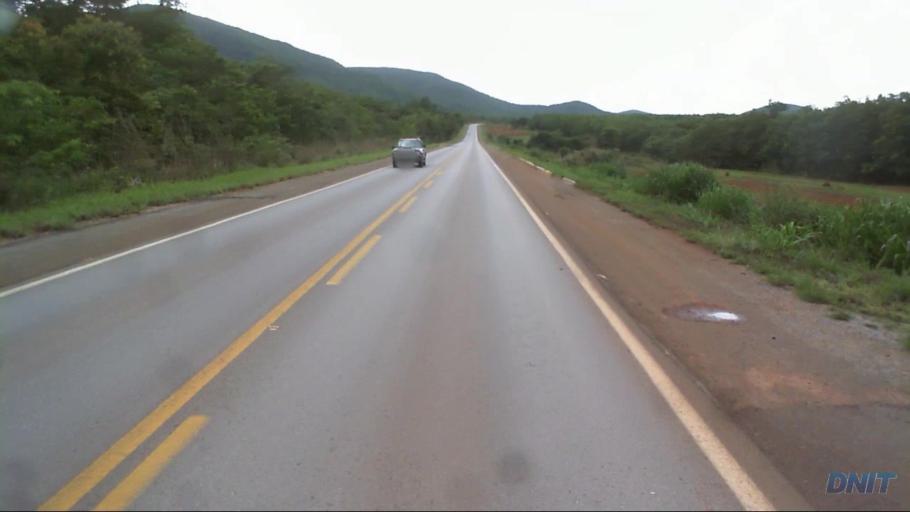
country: BR
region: Goias
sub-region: Barro Alto
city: Barro Alto
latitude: -14.8931
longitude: -48.9730
